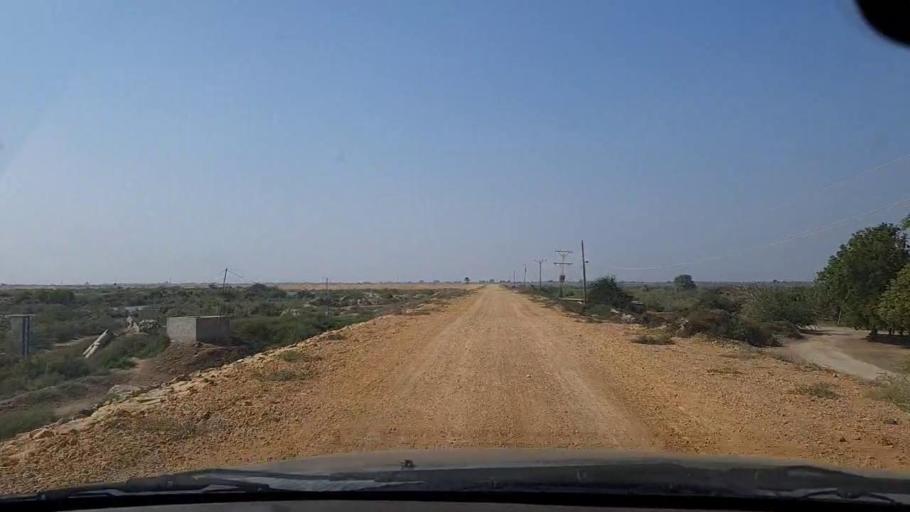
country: PK
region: Sindh
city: Chuhar Jamali
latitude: 24.4624
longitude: 67.8849
